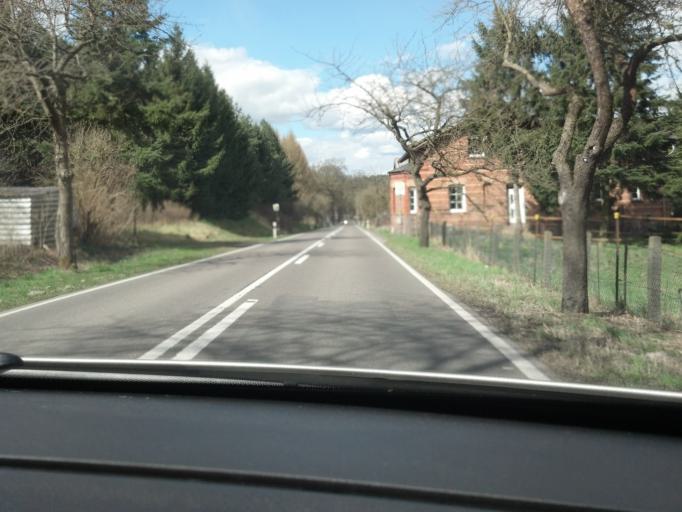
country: DE
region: Mecklenburg-Vorpommern
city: Burg Stargard
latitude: 53.4841
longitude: 13.3326
